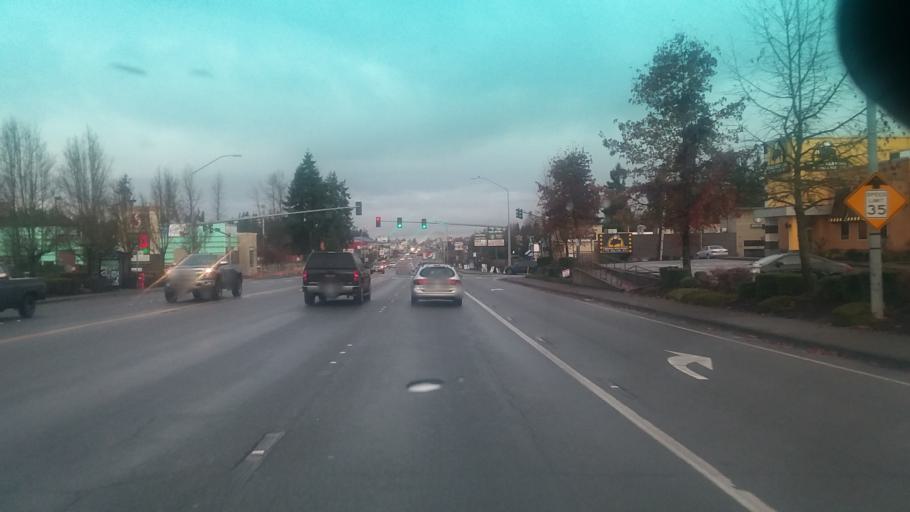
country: US
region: Washington
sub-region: Pierce County
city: South Hill
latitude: 47.1358
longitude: -122.2929
